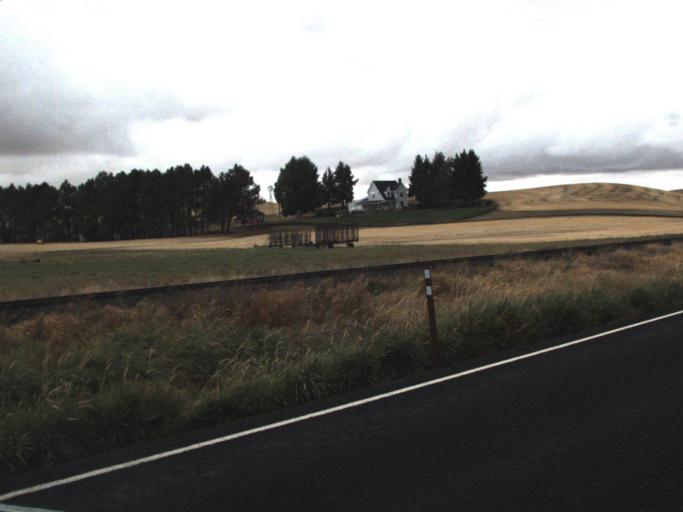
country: US
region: Washington
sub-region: Whitman County
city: Colfax
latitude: 47.1585
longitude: -117.2652
